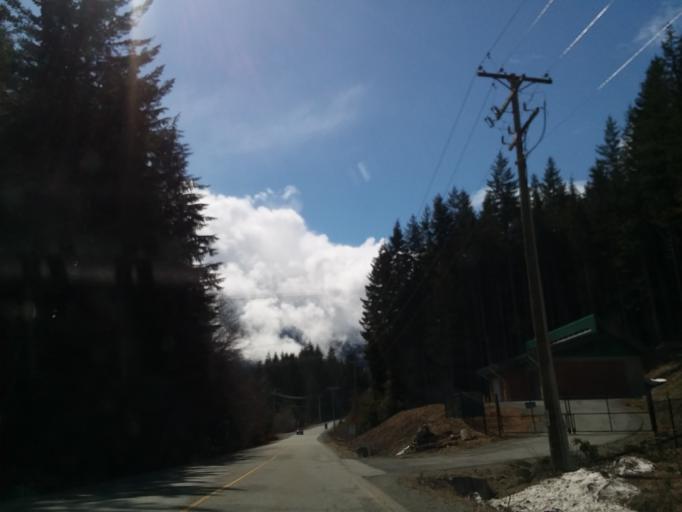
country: CA
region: British Columbia
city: Whistler
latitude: 50.1229
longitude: -122.9860
